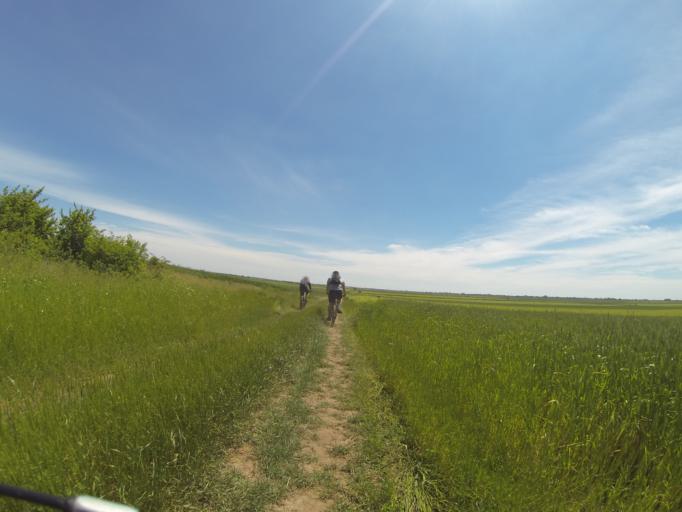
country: RO
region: Dolj
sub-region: Comuna Leu
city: Zanoaga
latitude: 44.1805
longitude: 24.0777
